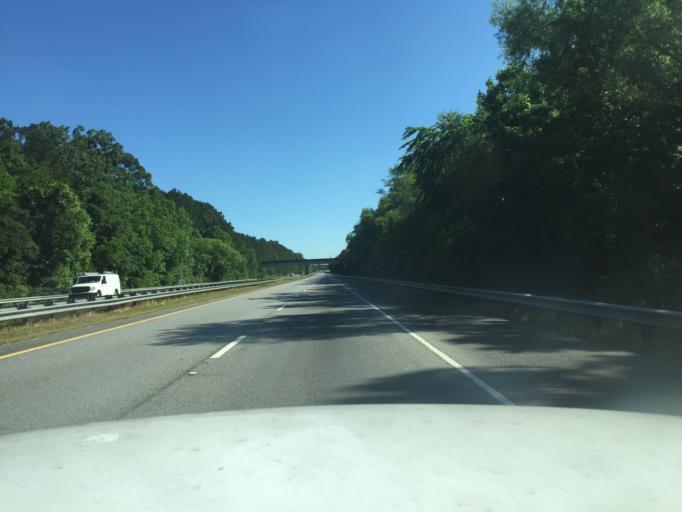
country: US
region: Georgia
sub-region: Chatham County
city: Georgetown
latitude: 32.0256
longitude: -81.1704
